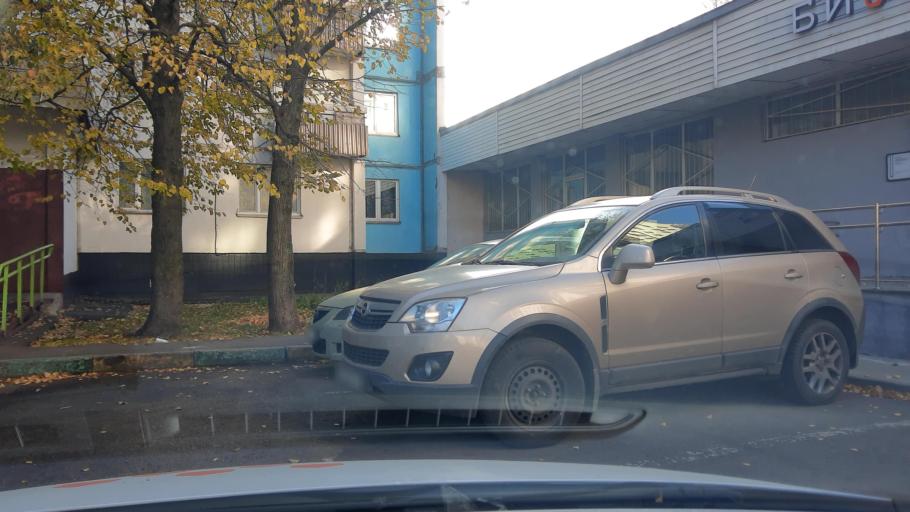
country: RU
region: Moscow
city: Biryulevo
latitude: 55.5785
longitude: 37.6835
